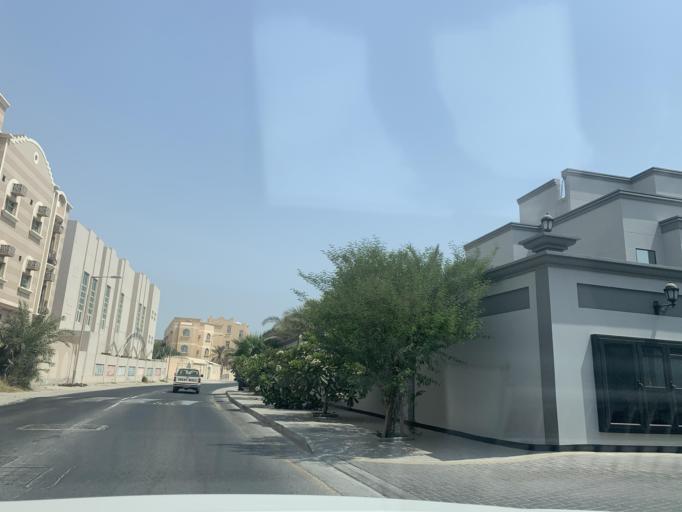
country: BH
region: Manama
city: Jidd Hafs
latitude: 26.2179
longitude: 50.4993
